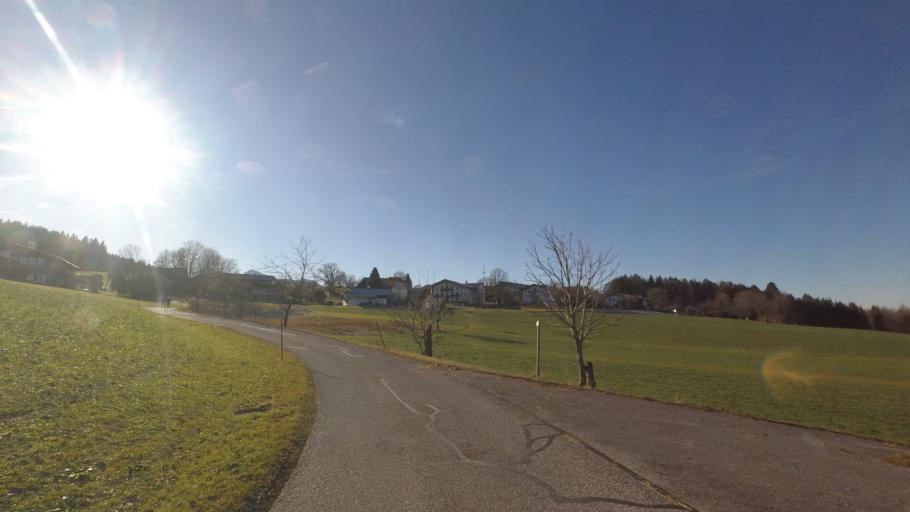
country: DE
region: Bavaria
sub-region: Upper Bavaria
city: Grabenstatt
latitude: 47.8355
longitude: 12.5636
